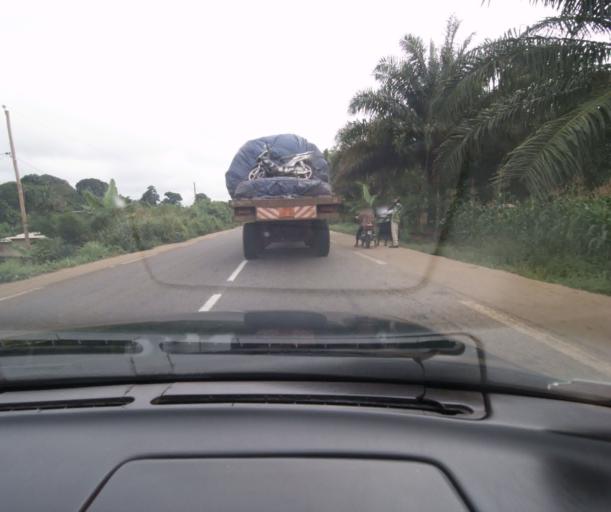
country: CM
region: Centre
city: Ombesa
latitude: 4.5874
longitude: 11.2644
